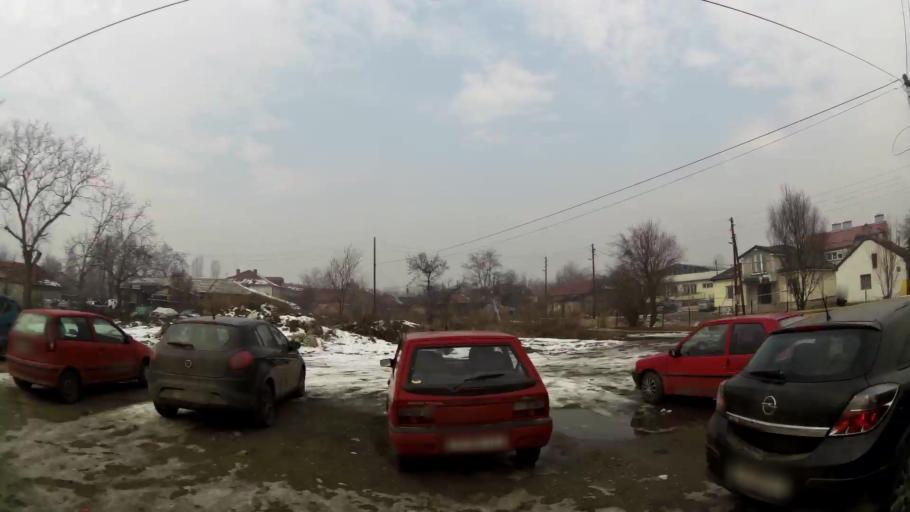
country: MK
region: Cair
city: Cair
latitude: 41.9957
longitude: 21.4613
